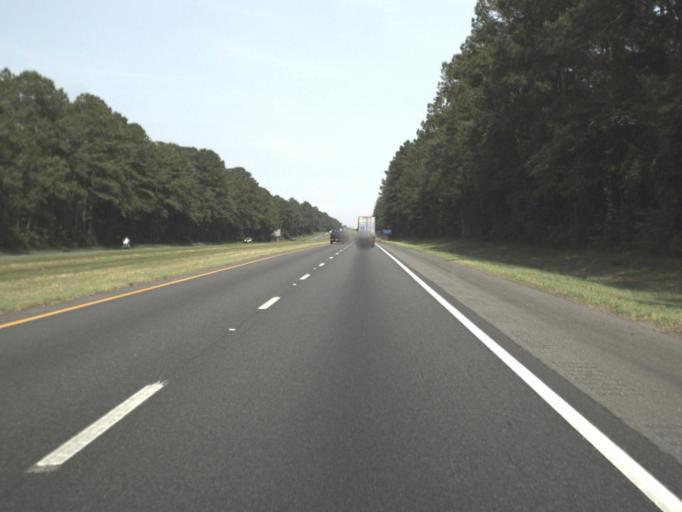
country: US
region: Florida
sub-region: Baker County
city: Macclenny
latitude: 30.2605
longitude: -82.1485
